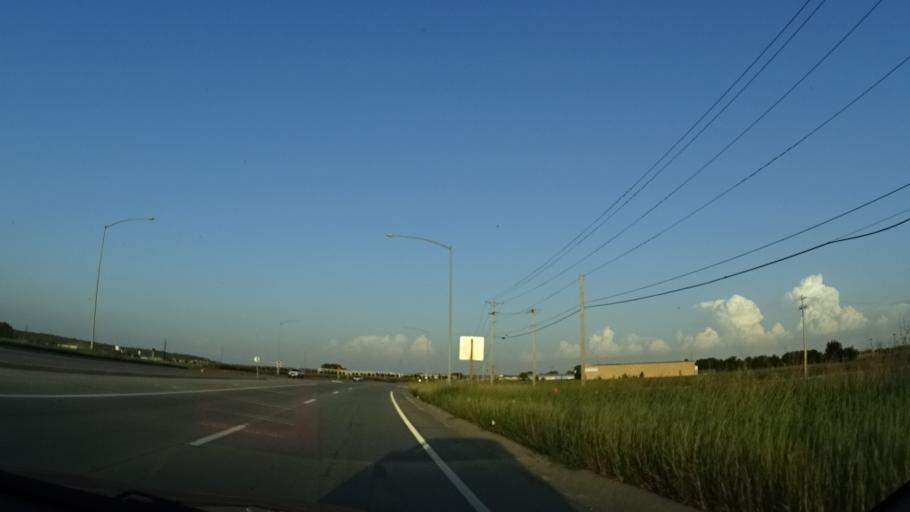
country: US
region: Iowa
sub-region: Pottawattamie County
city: Council Bluffs
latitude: 41.2195
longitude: -95.8760
